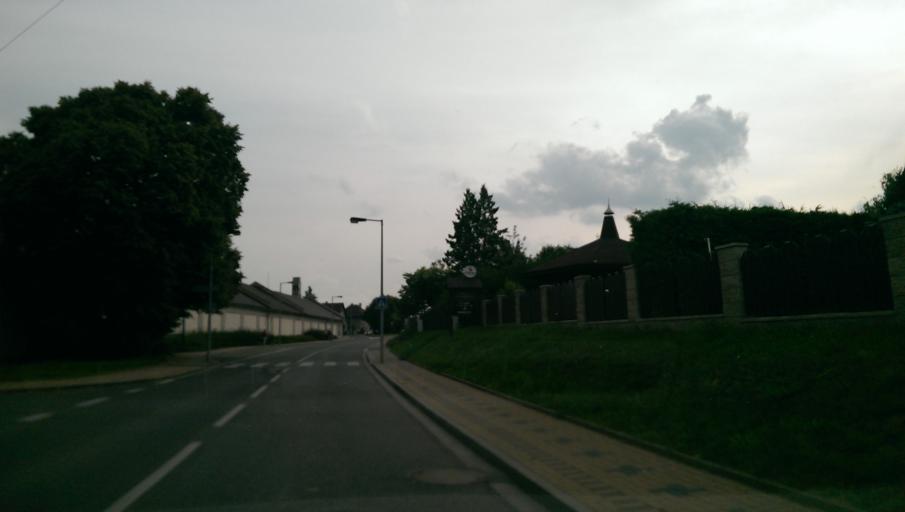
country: CZ
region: Liberecky
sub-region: Okres Semily
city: Turnov
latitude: 50.5981
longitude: 15.1555
